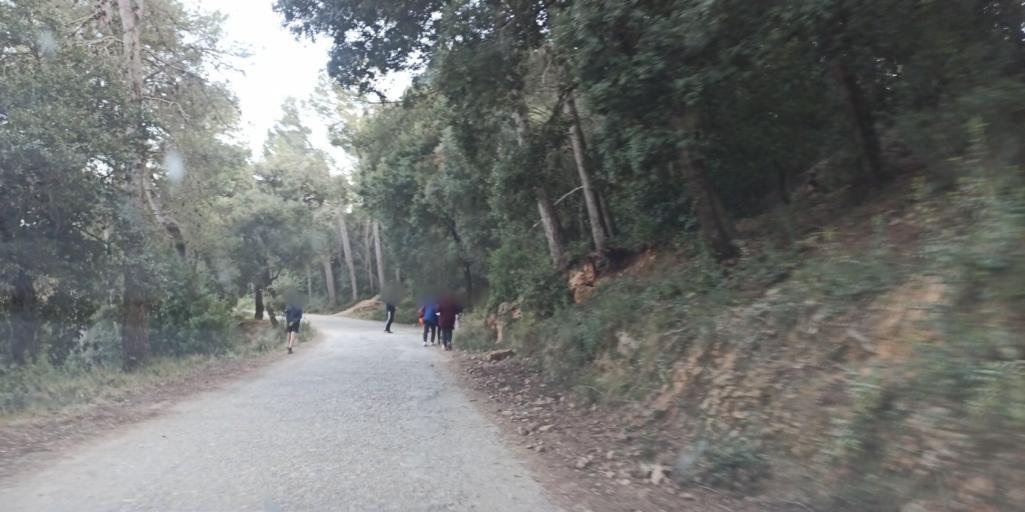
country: ES
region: Catalonia
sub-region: Provincia de Barcelona
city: Sant Feliu de Llobregat
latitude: 41.4141
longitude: 2.0572
